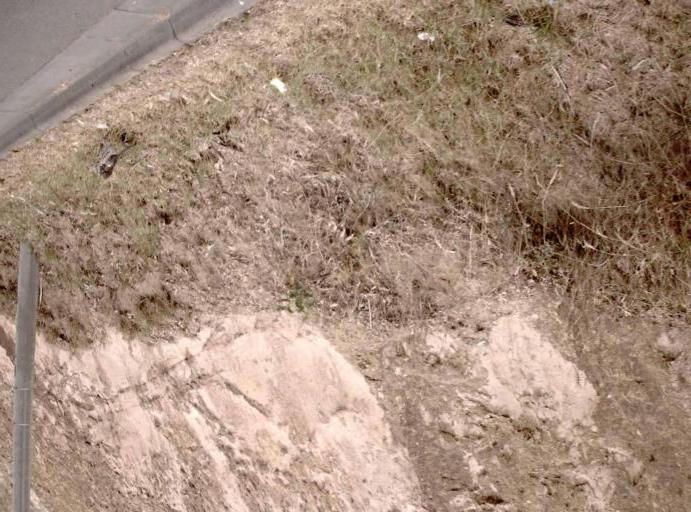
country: AU
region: Victoria
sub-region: Manningham
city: Bulleen
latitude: -37.7685
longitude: 145.0655
